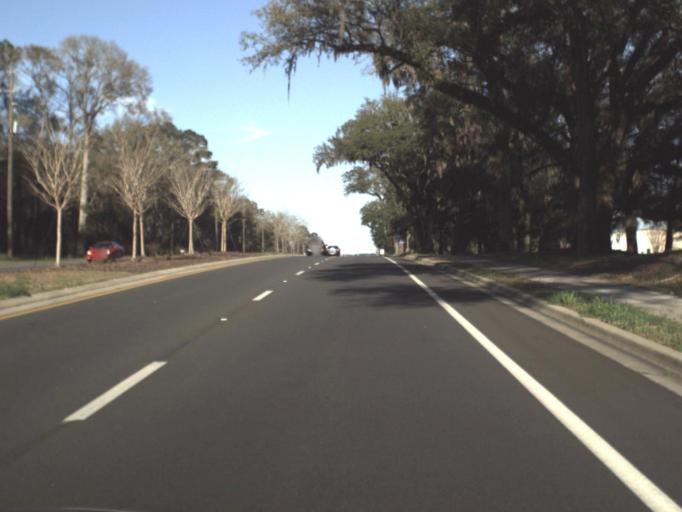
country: US
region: Florida
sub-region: Leon County
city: Tallahassee
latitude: 30.4789
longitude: -84.1756
